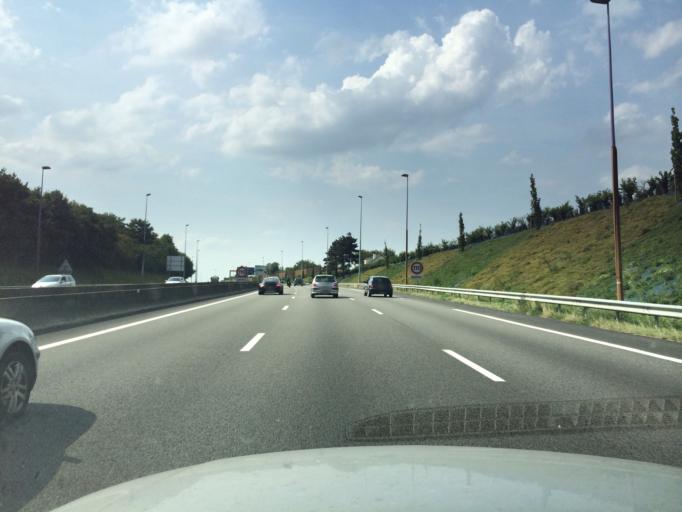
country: FR
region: Ile-de-France
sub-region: Departement des Yvelines
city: Mantes-la-Jolie
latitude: 48.9735
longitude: 1.7293
